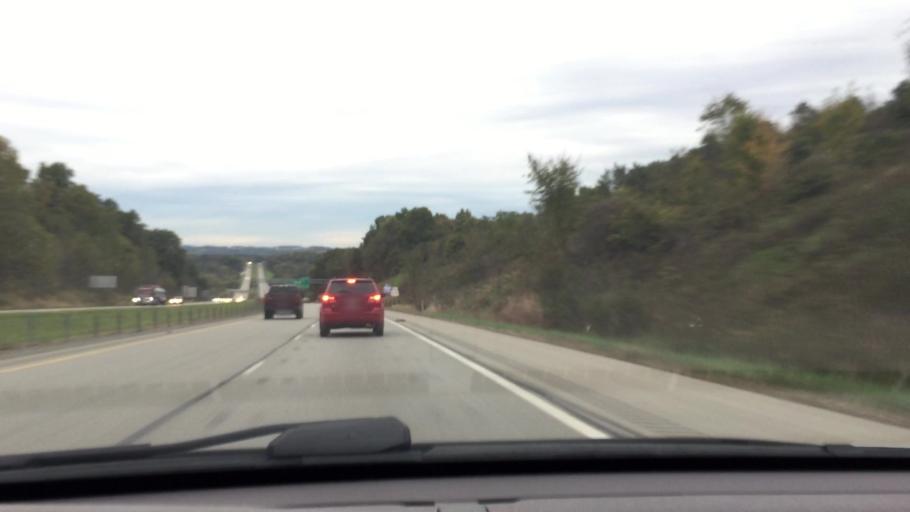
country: US
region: Pennsylvania
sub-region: Lawrence County
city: Oakwood
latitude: 41.0184
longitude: -80.3894
